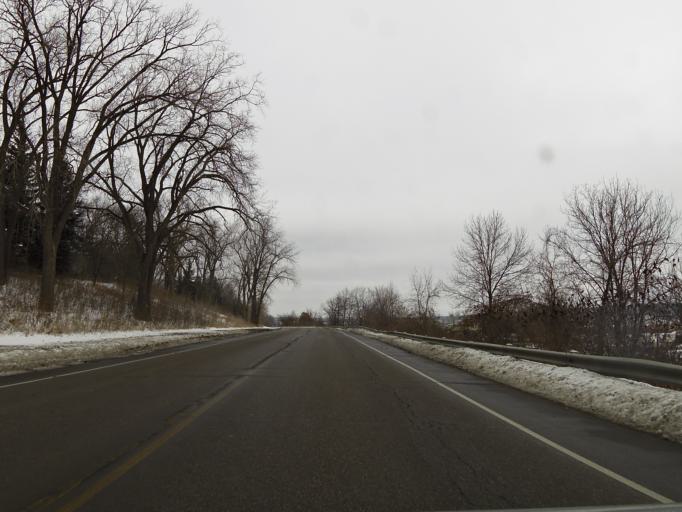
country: US
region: Minnesota
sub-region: Dakota County
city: South Saint Paul
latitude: 44.9206
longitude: -93.0605
